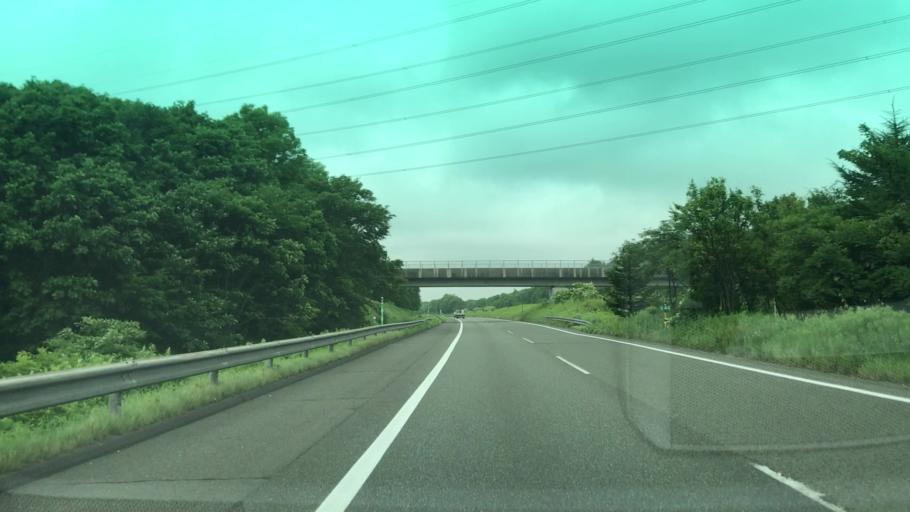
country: JP
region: Hokkaido
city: Chitose
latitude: 42.7382
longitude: 141.6517
